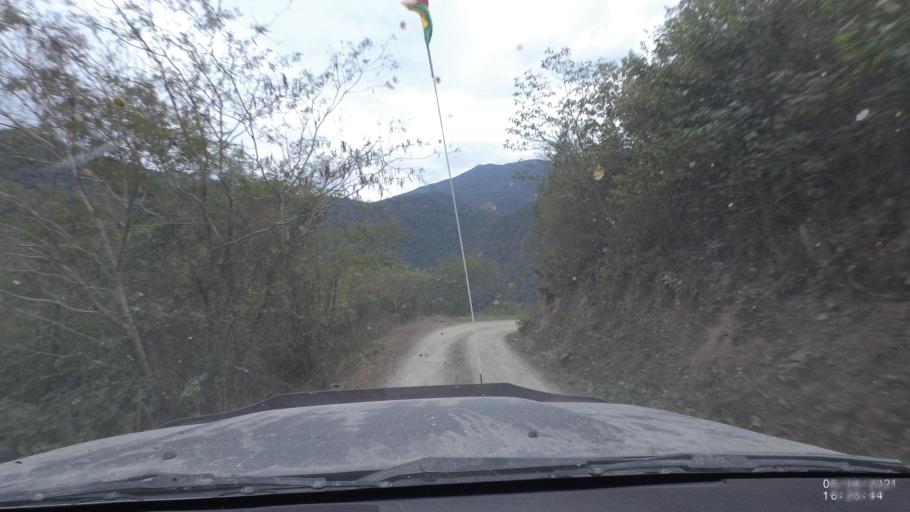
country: BO
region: La Paz
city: Quime
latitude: -16.5314
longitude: -66.7562
